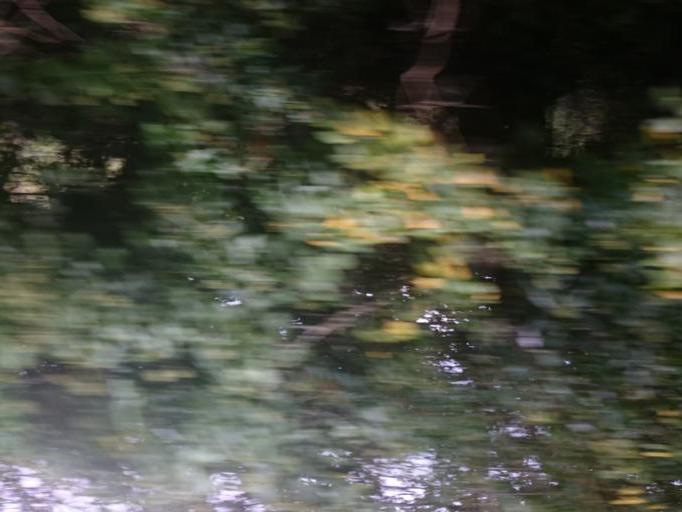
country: GB
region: England
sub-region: Gloucestershire
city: Coates
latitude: 51.7688
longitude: -2.0468
